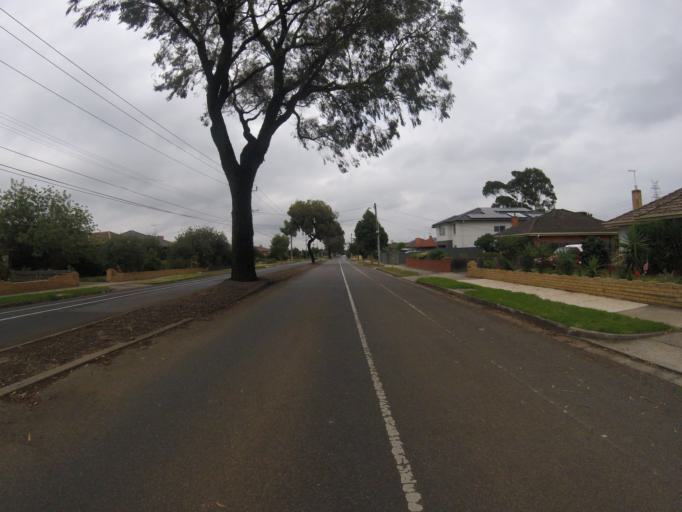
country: AU
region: Victoria
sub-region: Darebin
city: Reservoir
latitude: -37.7025
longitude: 145.0017
